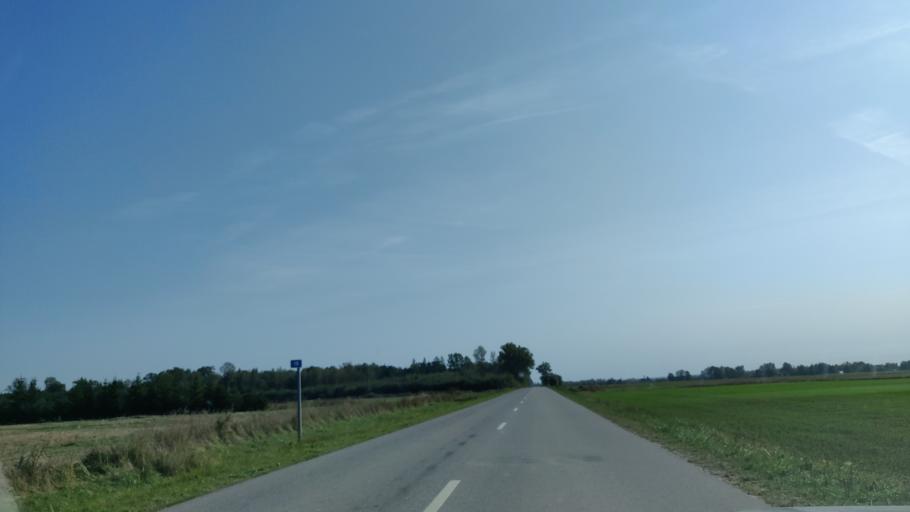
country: LT
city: Sirvintos
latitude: 54.9715
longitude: 24.8176
